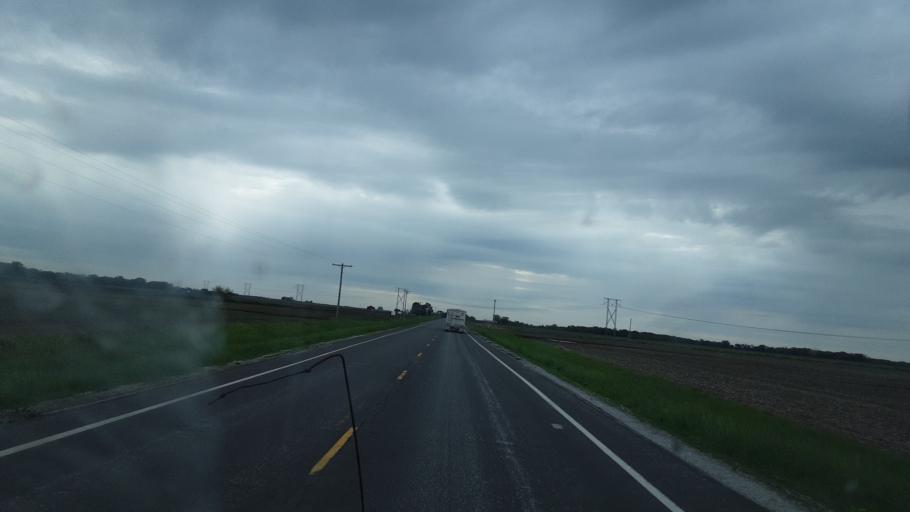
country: US
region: Illinois
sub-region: Fulton County
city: Astoria
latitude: 40.3487
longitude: -90.3068
